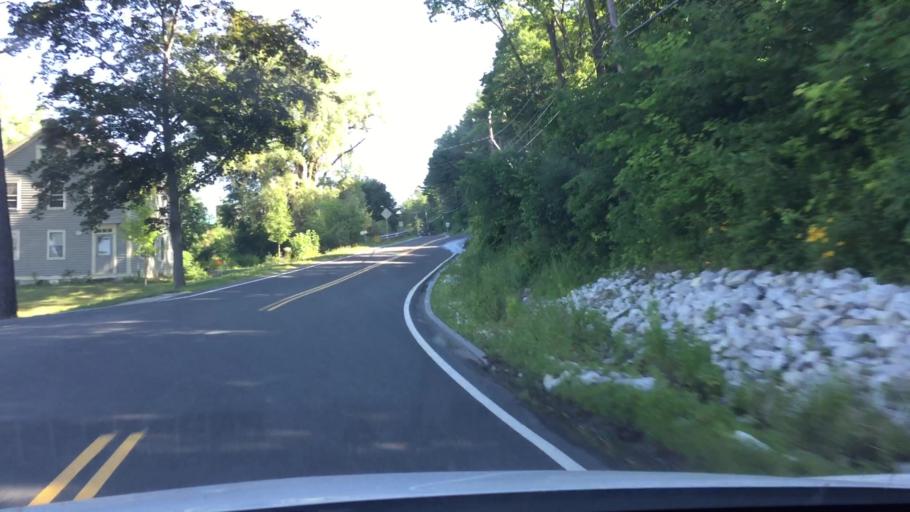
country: US
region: Massachusetts
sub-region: Berkshire County
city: Lee
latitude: 42.2739
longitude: -73.2384
